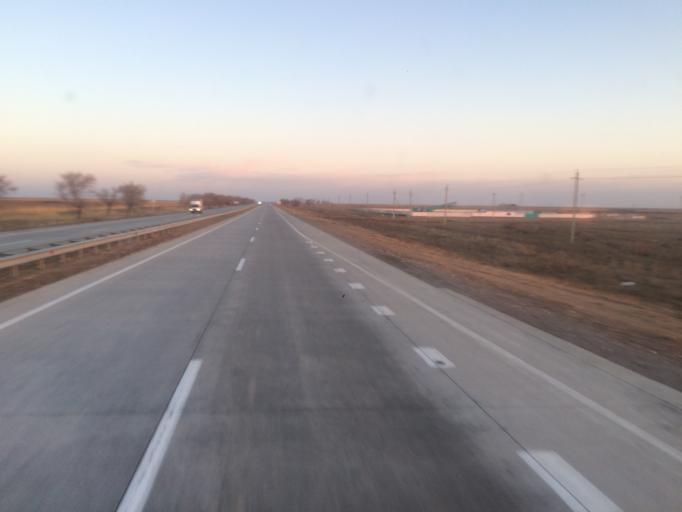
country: KZ
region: Ongtustik Qazaqstan
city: Bayaldyr
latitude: 43.0600
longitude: 68.6845
